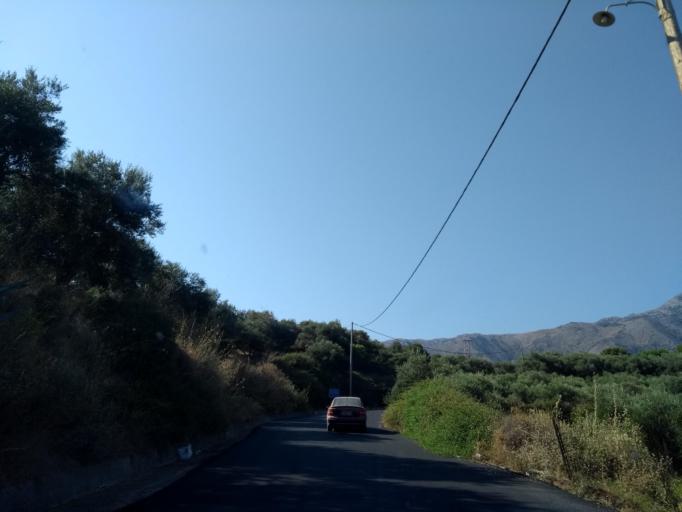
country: GR
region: Crete
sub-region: Nomos Chanias
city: Georgioupolis
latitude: 35.3226
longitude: 24.2999
